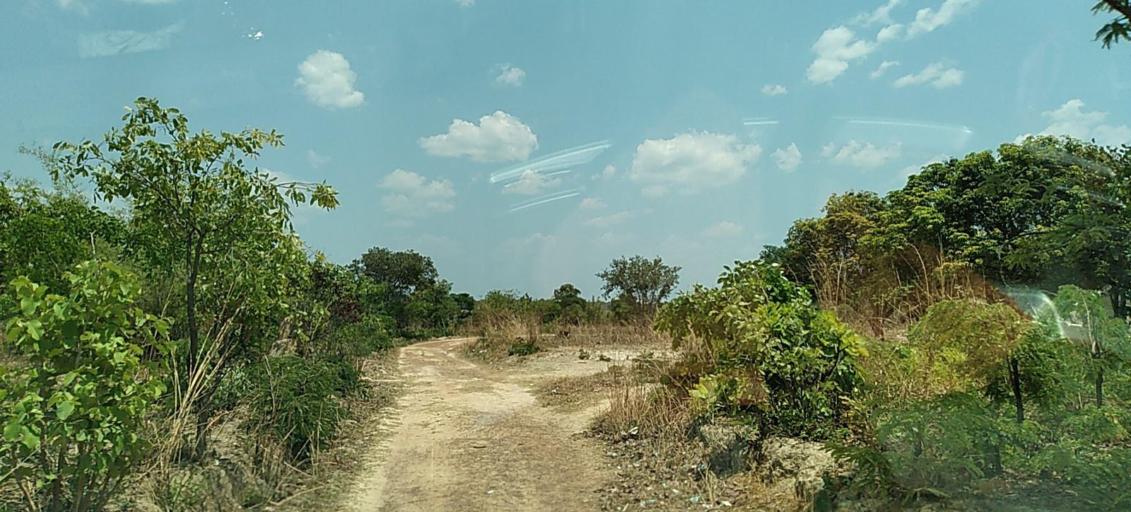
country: ZM
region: Copperbelt
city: Chililabombwe
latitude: -12.4780
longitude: 27.6661
